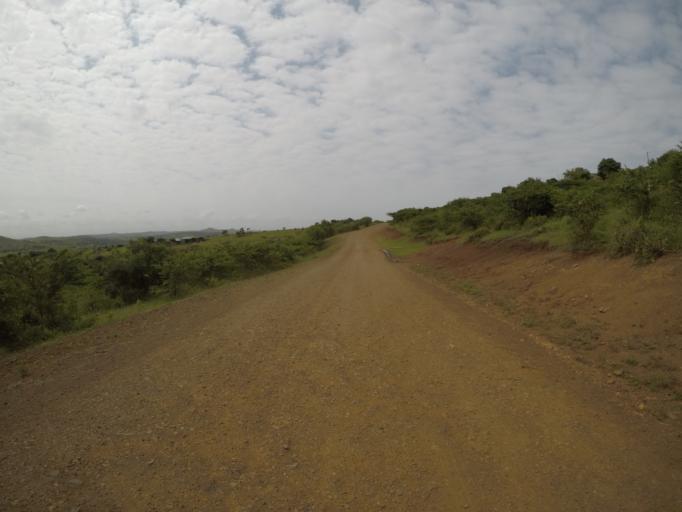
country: ZA
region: KwaZulu-Natal
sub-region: uThungulu District Municipality
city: Empangeni
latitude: -28.6224
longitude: 31.9060
